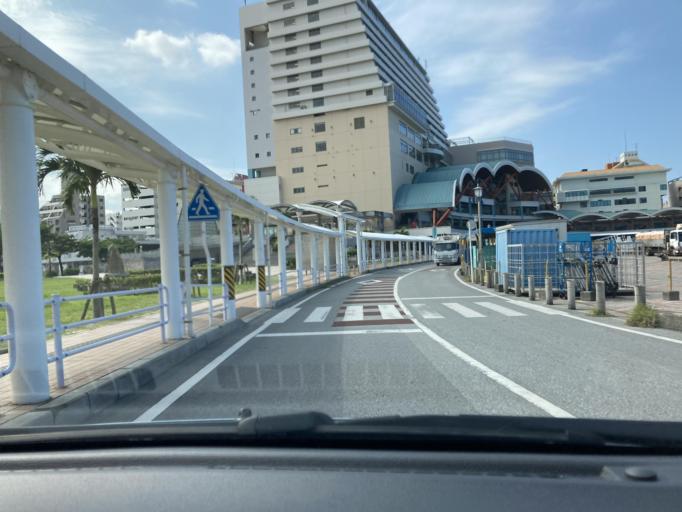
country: JP
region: Okinawa
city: Naha-shi
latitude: 26.2251
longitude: 127.6840
